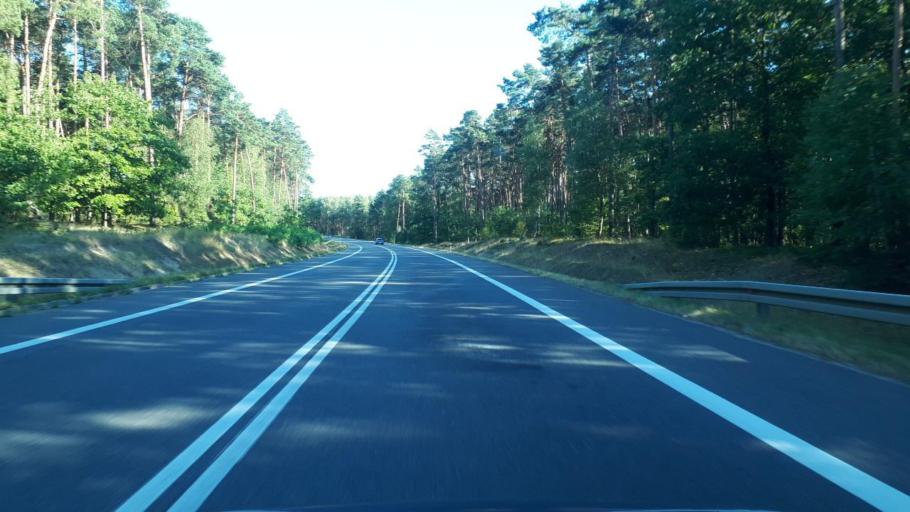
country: PL
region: Silesian Voivodeship
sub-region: Powiat lubliniecki
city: Lubliniec
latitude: 50.6615
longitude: 18.6539
